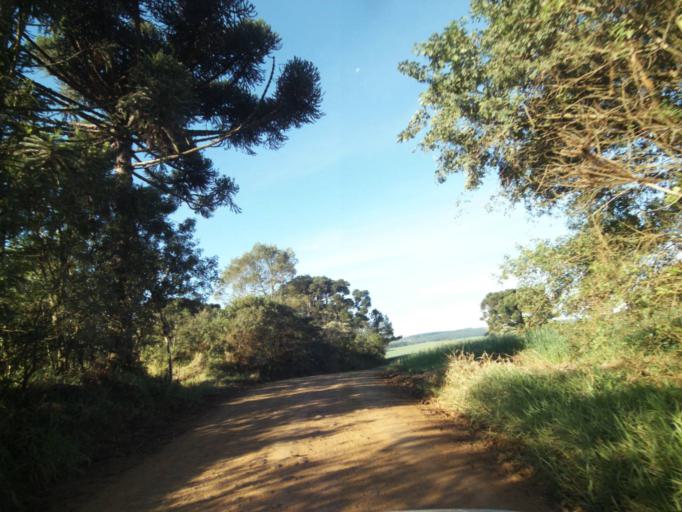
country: BR
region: Parana
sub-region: Tibagi
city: Tibagi
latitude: -24.5408
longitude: -50.6112
